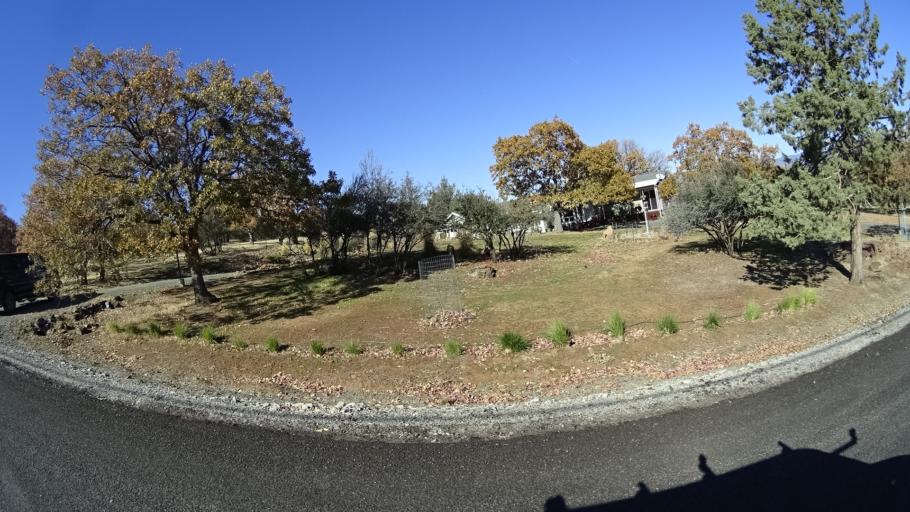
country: US
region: California
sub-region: Siskiyou County
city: Montague
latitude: 41.8764
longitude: -122.4833
